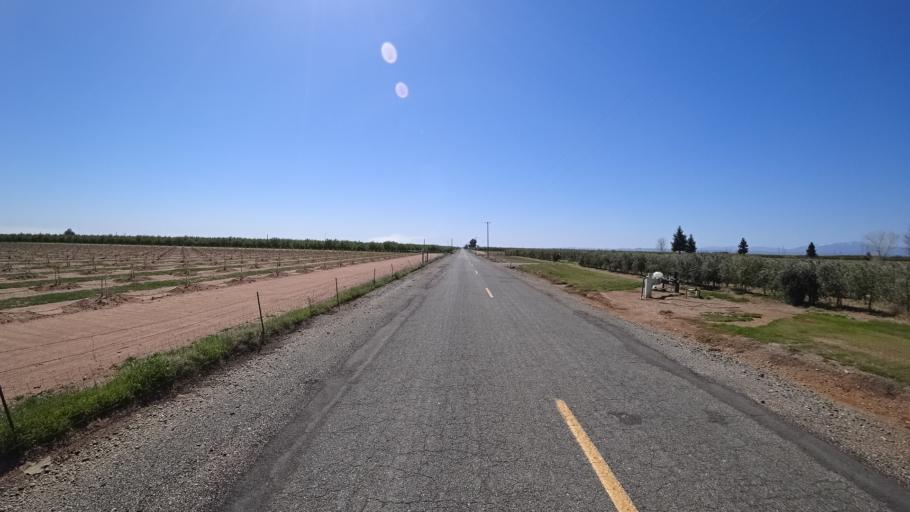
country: US
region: California
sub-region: Glenn County
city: Orland
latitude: 39.6767
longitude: -122.2531
